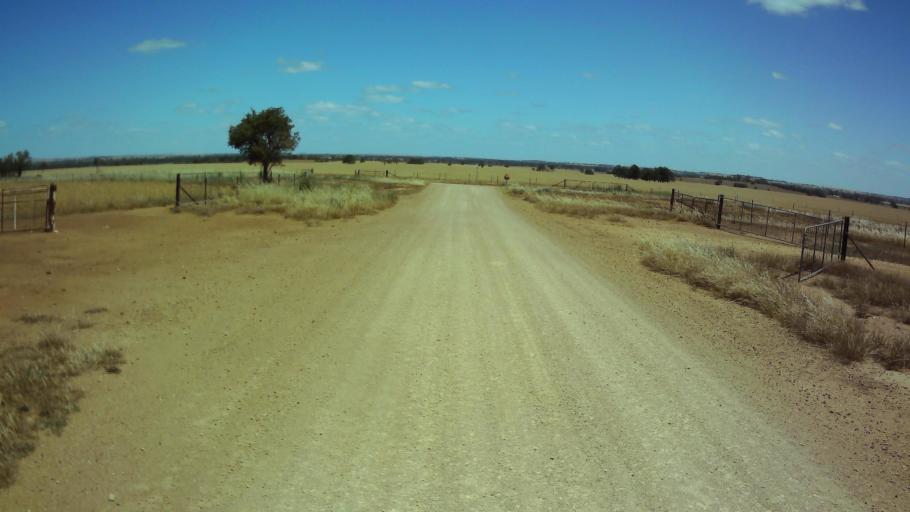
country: AU
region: New South Wales
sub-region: Weddin
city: Grenfell
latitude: -33.9780
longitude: 148.3266
